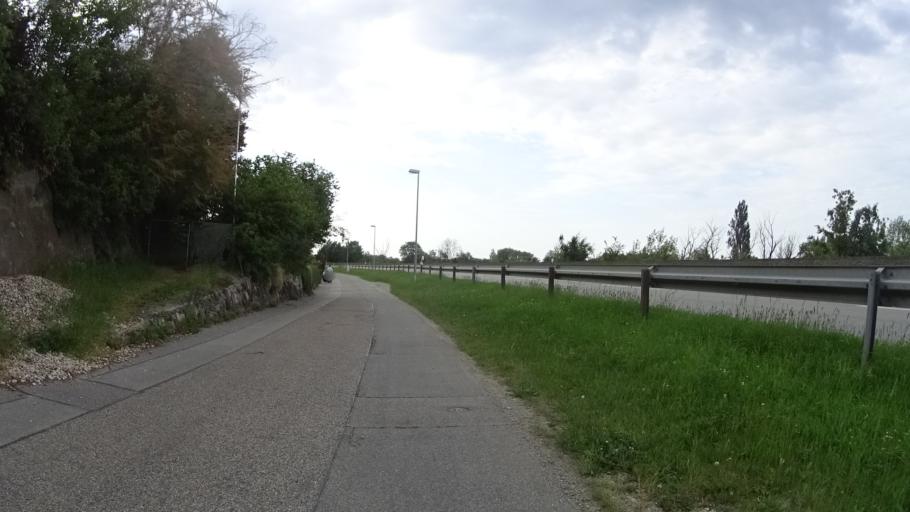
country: DE
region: Bavaria
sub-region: Lower Bavaria
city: Bogen
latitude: 48.9011
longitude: 12.6944
